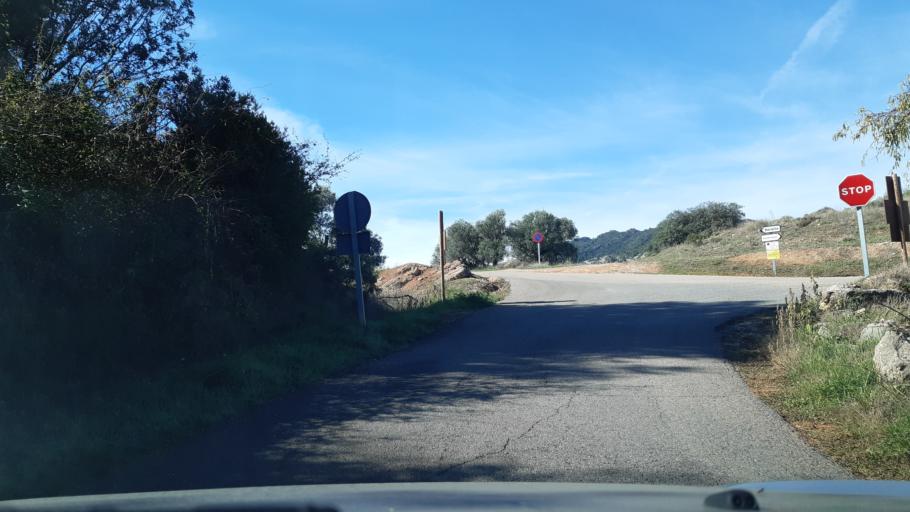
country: ES
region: Aragon
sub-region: Provincia de Teruel
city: Valderrobres
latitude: 40.8345
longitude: 0.1900
